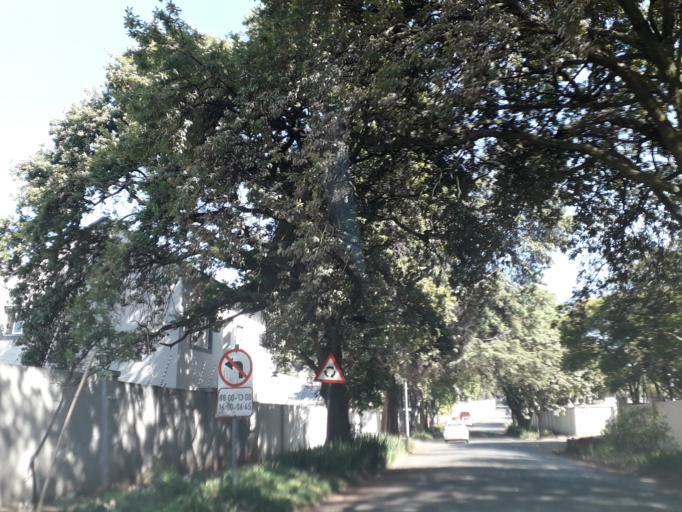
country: ZA
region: Gauteng
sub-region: City of Johannesburg Metropolitan Municipality
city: Johannesburg
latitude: -26.1752
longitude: 28.0608
